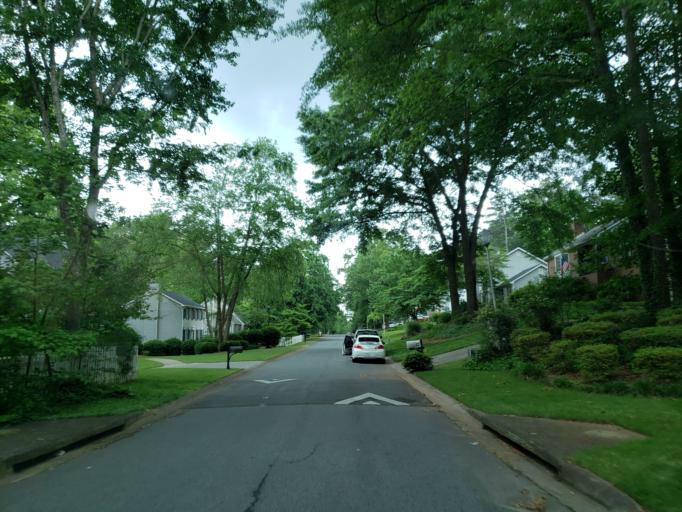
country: US
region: Georgia
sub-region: Cobb County
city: Marietta
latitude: 33.9588
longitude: -84.5707
